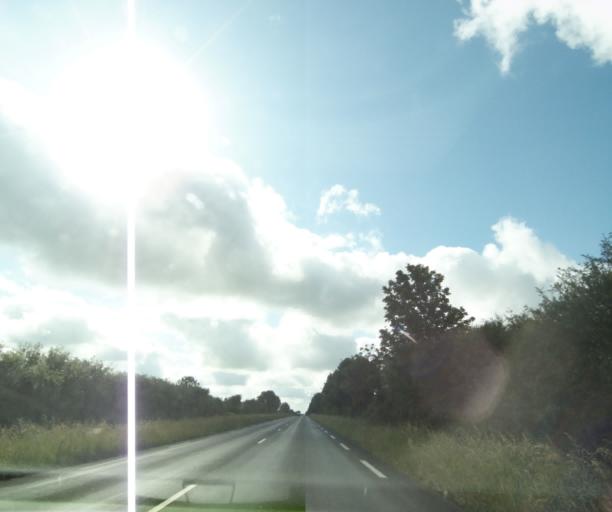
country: FR
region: Pays de la Loire
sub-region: Departement de la Sarthe
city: Vion
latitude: 47.8069
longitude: -0.2757
